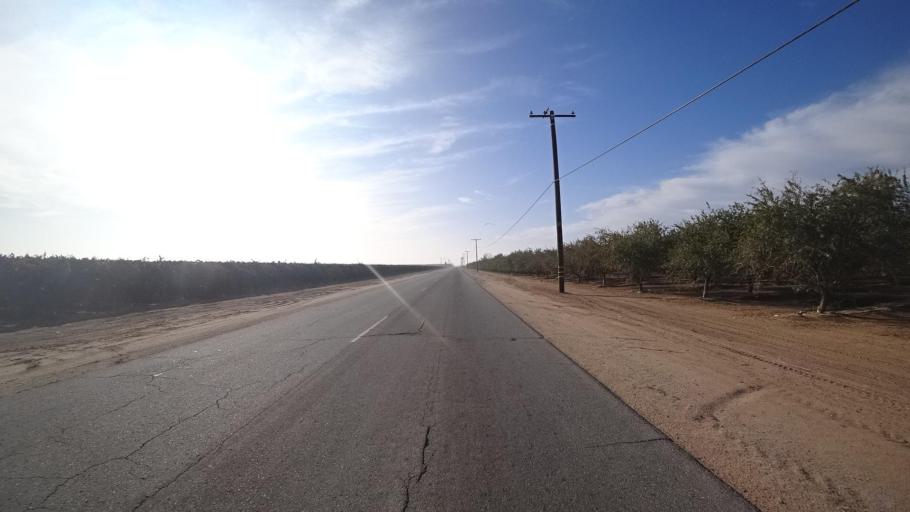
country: US
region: California
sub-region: Kern County
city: McFarland
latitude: 35.6644
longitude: -119.2047
